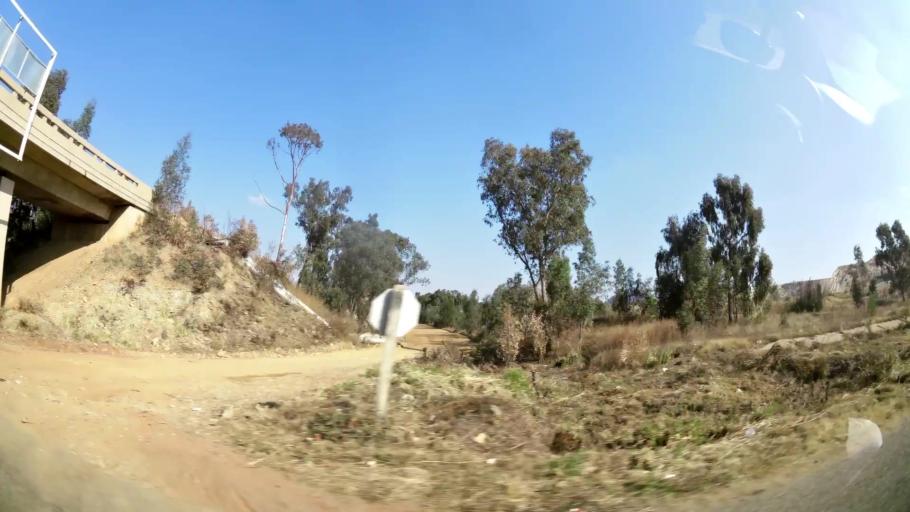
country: ZA
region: Gauteng
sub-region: West Rand District Municipality
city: Randfontein
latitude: -26.1809
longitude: 27.7206
